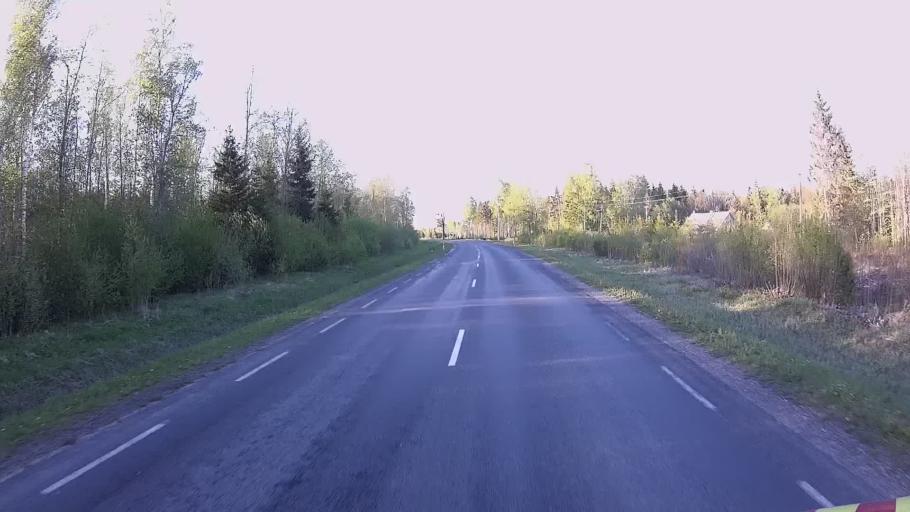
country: EE
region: Viljandimaa
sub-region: Viiratsi vald
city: Viiratsi
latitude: 58.4578
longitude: 25.7480
